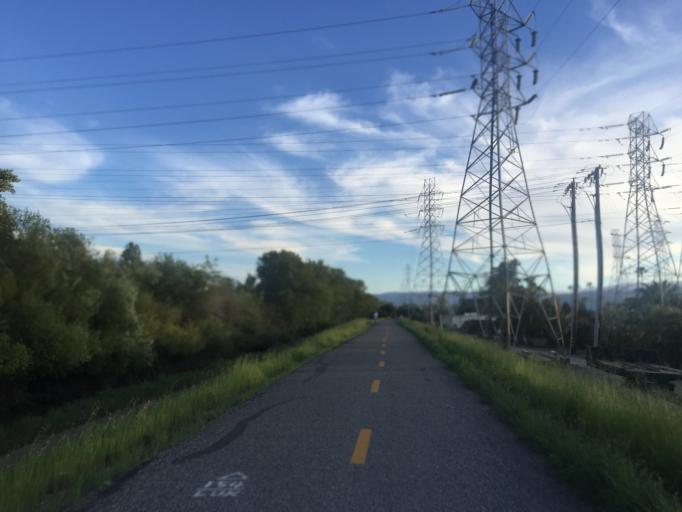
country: US
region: California
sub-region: Santa Clara County
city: Mountain View
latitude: 37.4184
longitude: -122.0689
